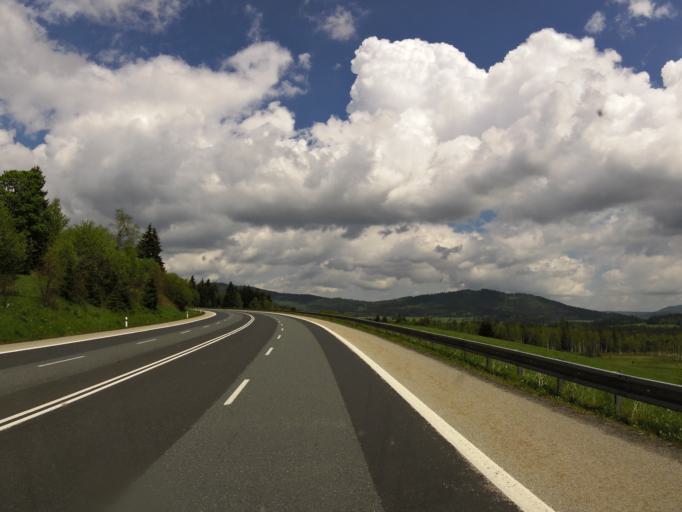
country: DE
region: Bavaria
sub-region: Lower Bavaria
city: Philippsreut
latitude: 48.8926
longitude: 13.7259
